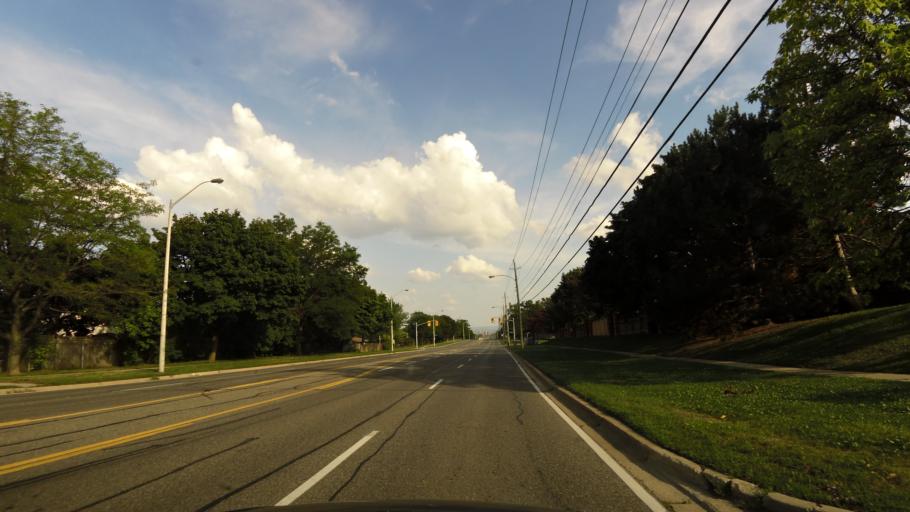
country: CA
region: Ontario
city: Burlington
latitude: 43.3623
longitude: -79.8512
